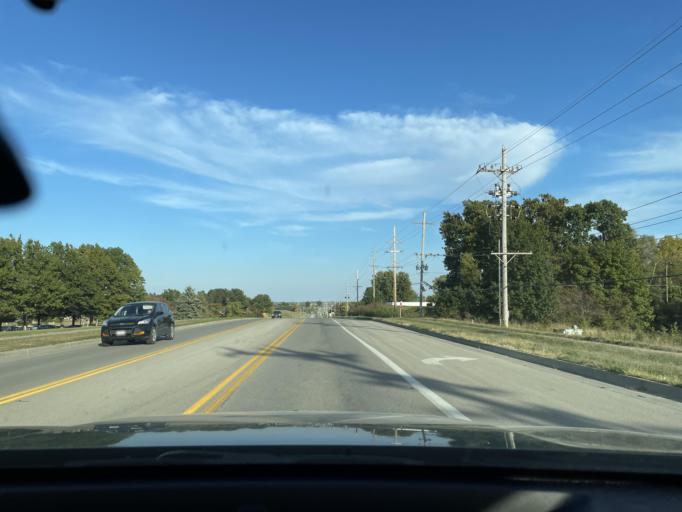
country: US
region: Missouri
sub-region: Buchanan County
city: Saint Joseph
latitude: 39.7553
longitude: -94.7883
